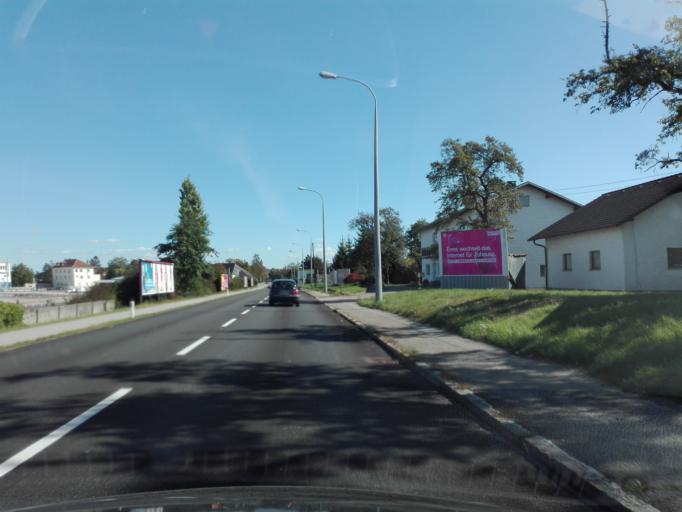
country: AT
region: Upper Austria
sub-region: Politischer Bezirk Linz-Land
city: Enns
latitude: 48.2167
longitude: 14.4504
